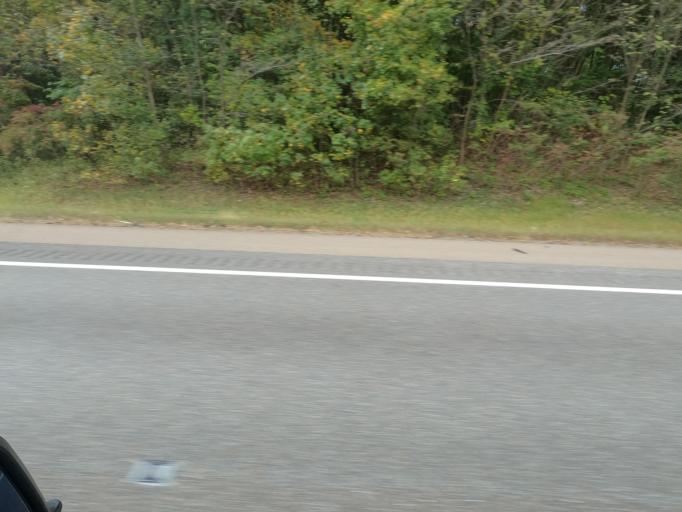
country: US
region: Tennessee
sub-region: Haywood County
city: Brownsville
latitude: 35.5316
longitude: -89.2574
